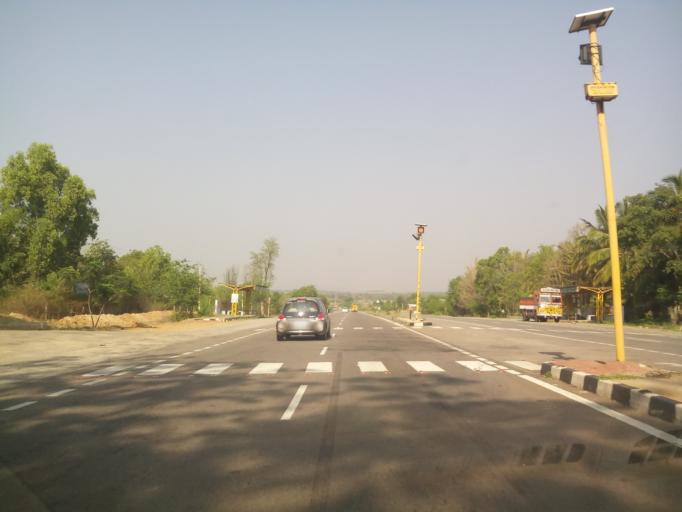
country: IN
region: Karnataka
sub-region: Tumkur
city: Kunigal
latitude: 12.9969
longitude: 76.9184
